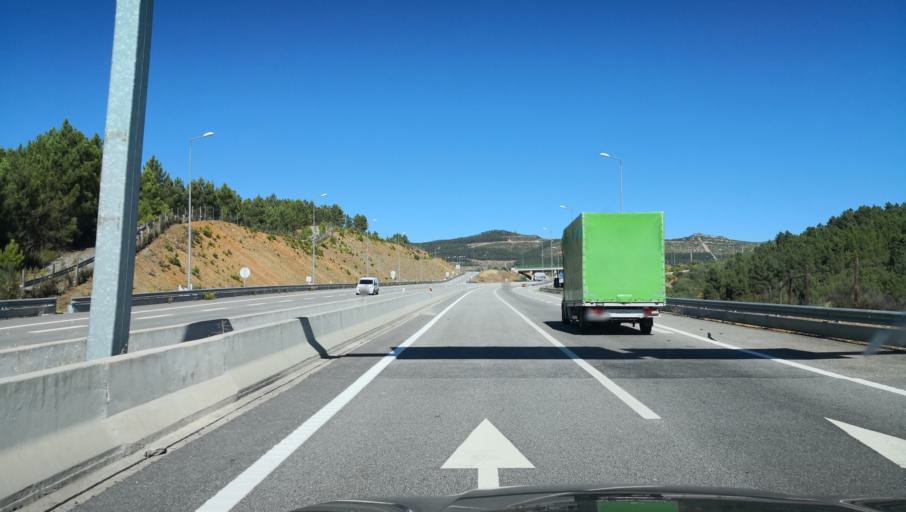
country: PT
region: Vila Real
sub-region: Murca
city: Murca
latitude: 41.4147
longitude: -7.4129
